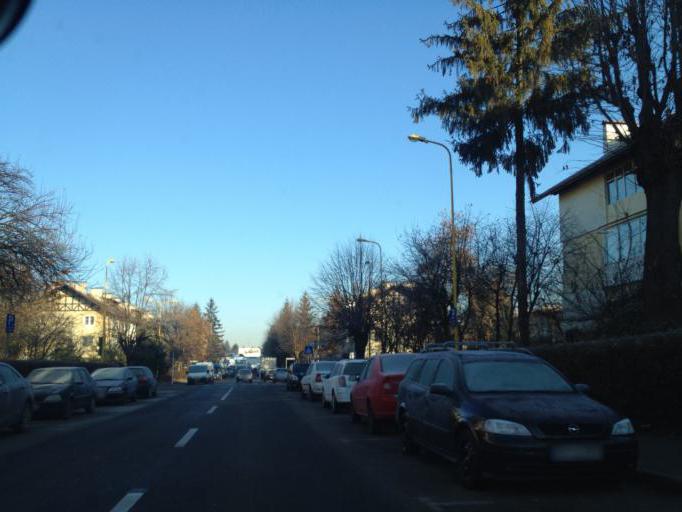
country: RO
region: Brasov
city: Brasov
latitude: 45.6396
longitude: 25.6311
